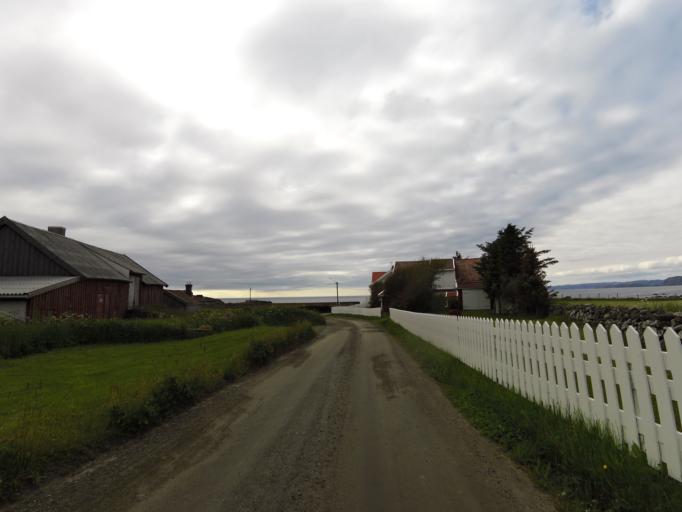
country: NO
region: Vest-Agder
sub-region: Farsund
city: Vestbygd
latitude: 58.1390
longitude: 6.6073
